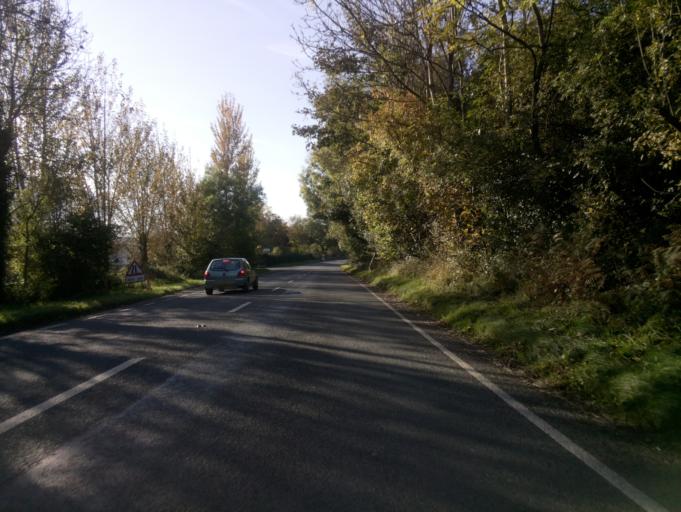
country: GB
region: England
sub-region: Herefordshire
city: Clifford
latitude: 52.1211
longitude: -3.0825
